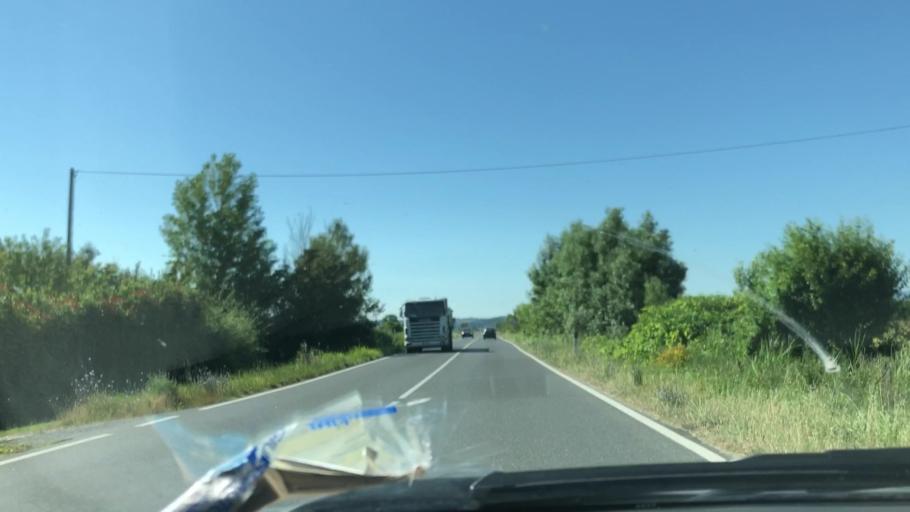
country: IT
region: Tuscany
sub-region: Province of Pisa
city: Forcoli
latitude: 43.5972
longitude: 10.6969
